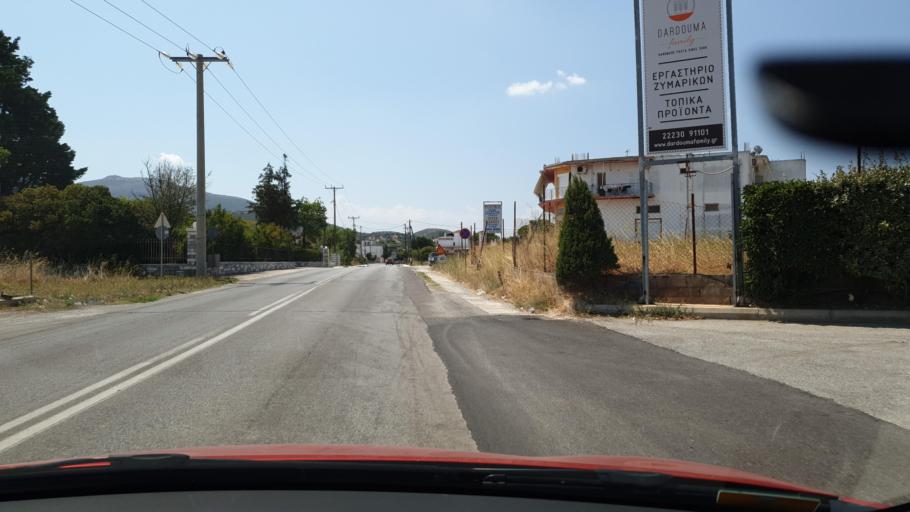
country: GR
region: Central Greece
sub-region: Nomos Evvoias
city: Aliveri
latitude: 38.3943
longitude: 24.0981
